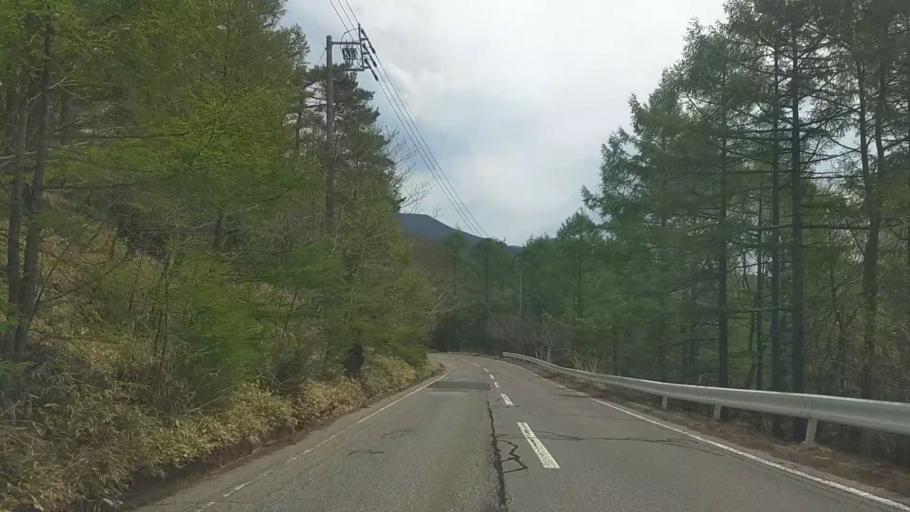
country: JP
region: Nagano
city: Chino
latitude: 36.0485
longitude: 138.3074
